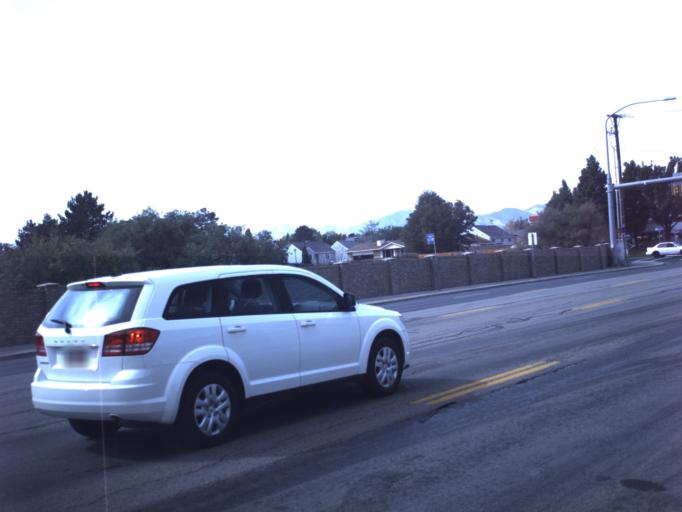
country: US
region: Utah
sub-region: Salt Lake County
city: Kearns
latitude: 40.6532
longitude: -111.9759
